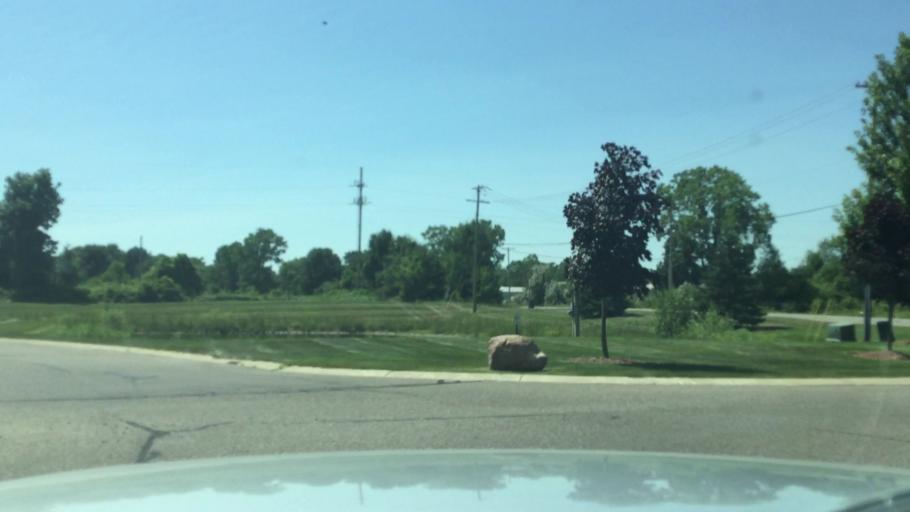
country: US
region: Michigan
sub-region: Genesee County
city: Swartz Creek
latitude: 42.9572
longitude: -83.8049
